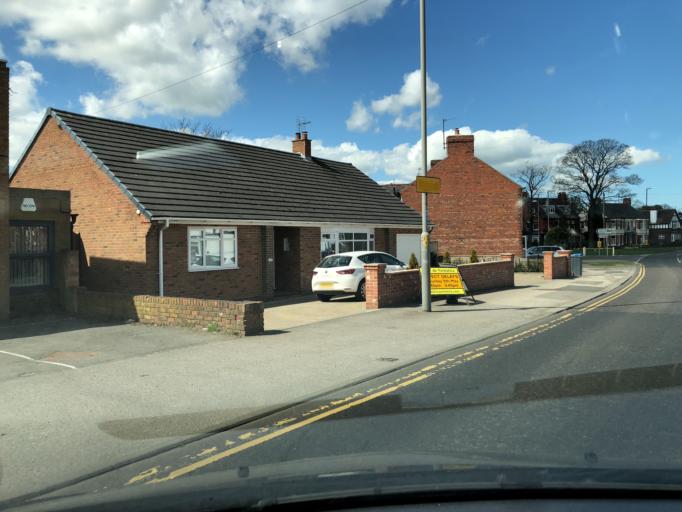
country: GB
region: England
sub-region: North Yorkshire
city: Northallerton
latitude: 54.3325
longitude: -1.4323
